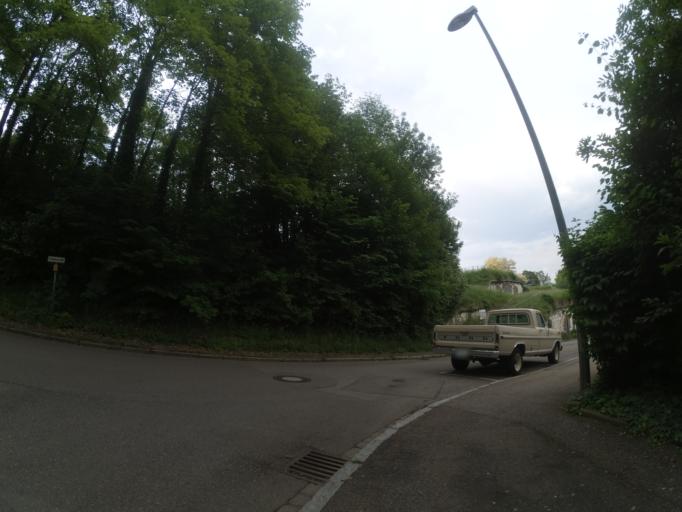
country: DE
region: Baden-Wuerttemberg
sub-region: Tuebingen Region
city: Ulm
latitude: 48.4116
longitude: 9.9868
